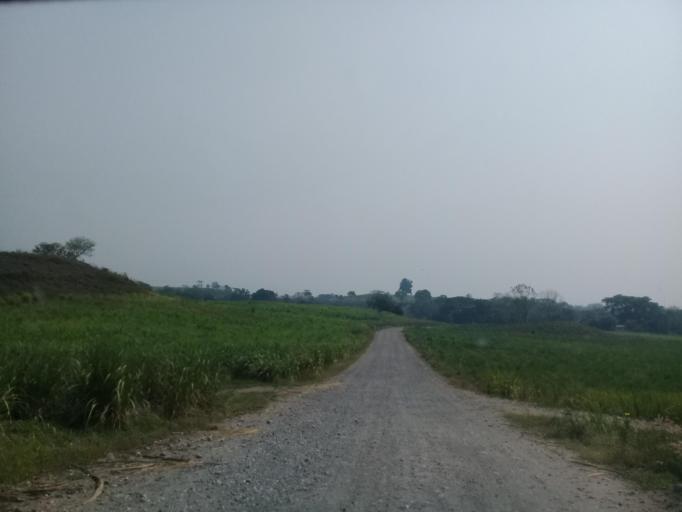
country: MX
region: Oaxaca
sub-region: Acatlan de Perez Figueroa
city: Zona Urbana Ejidal
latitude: 18.5857
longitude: -96.5647
